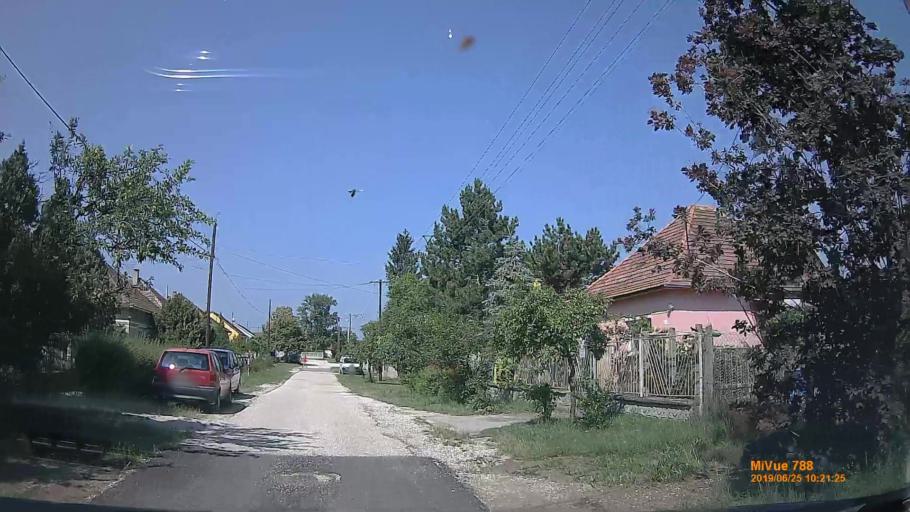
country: HU
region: Komarom-Esztergom
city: Dorog
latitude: 47.7355
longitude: 18.6987
